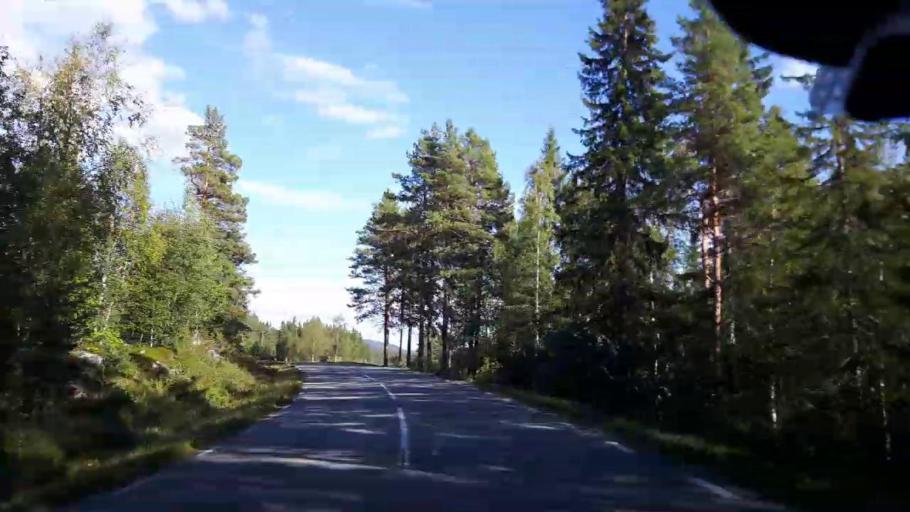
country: SE
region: Jaemtland
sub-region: Stroemsunds Kommun
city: Stroemsund
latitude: 63.3870
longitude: 15.5642
